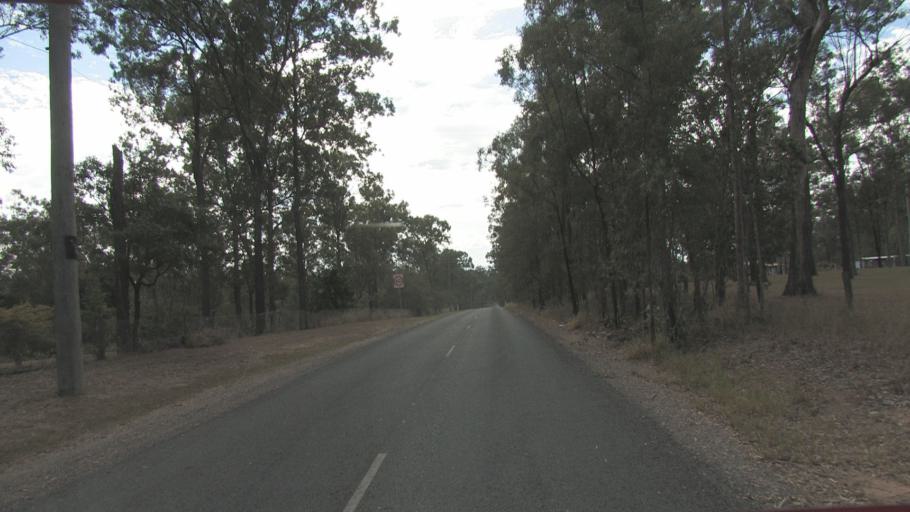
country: AU
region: Queensland
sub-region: Logan
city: North Maclean
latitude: -27.7648
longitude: 152.9701
